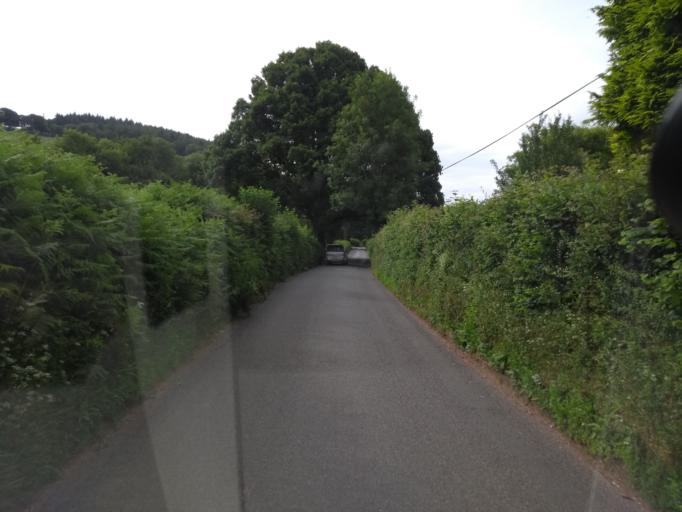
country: GB
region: England
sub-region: Somerset
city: Wiveliscombe
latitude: 51.1024
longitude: -3.3054
